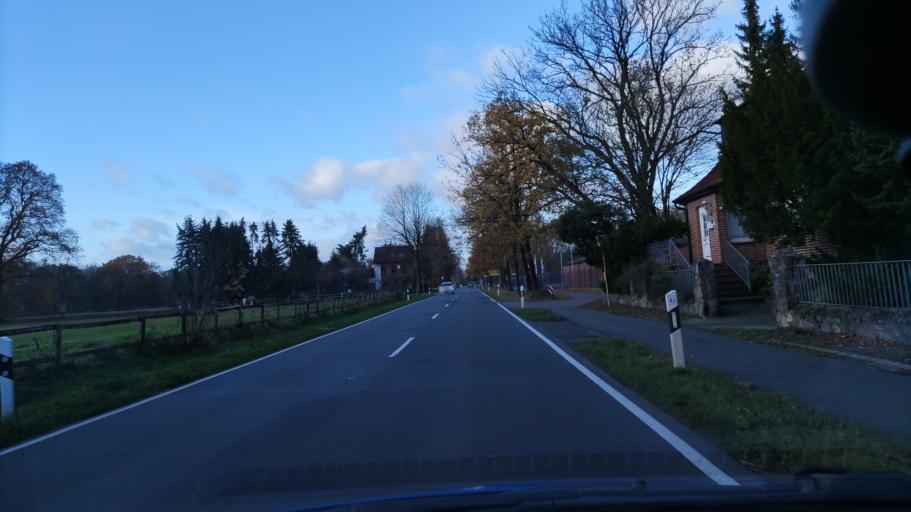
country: DE
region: Lower Saxony
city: Schneverdingen
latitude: 53.0753
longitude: 9.8132
